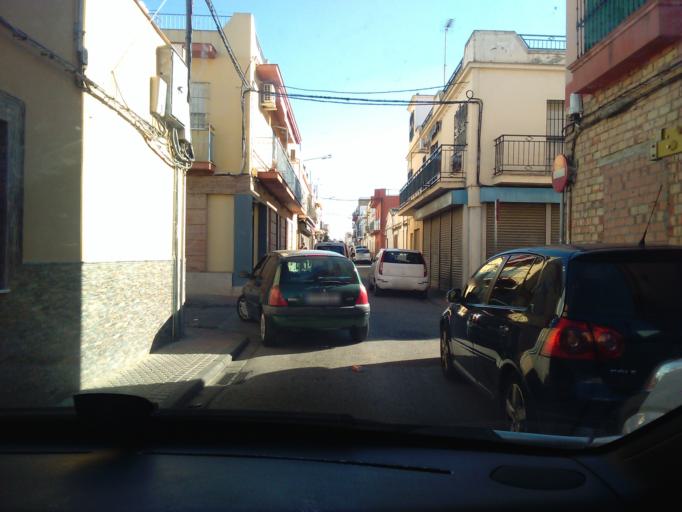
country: ES
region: Andalusia
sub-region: Provincia de Sevilla
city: Sevilla
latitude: 37.3847
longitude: -5.9077
